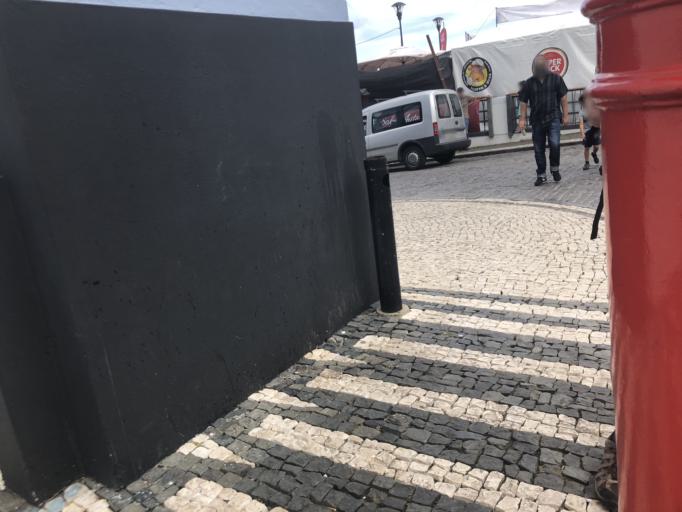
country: PT
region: Azores
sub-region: Angra do Heroismo
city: Angra do Heroismo
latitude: 38.6541
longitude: -27.2185
